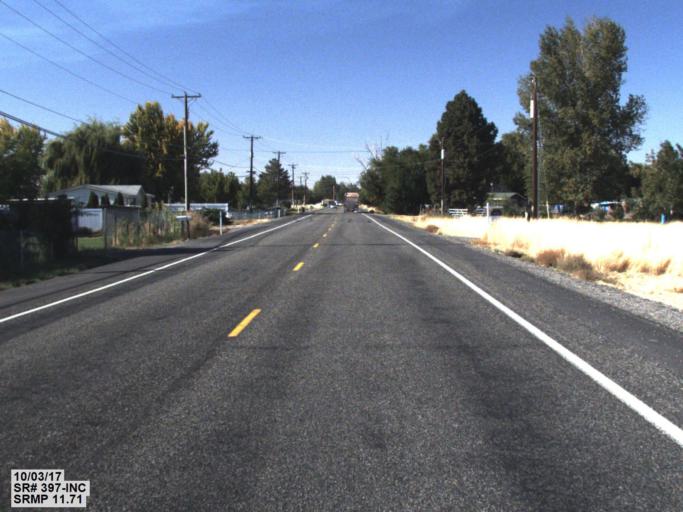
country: US
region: Washington
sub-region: Benton County
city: Finley
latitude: 46.1502
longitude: -119.0246
